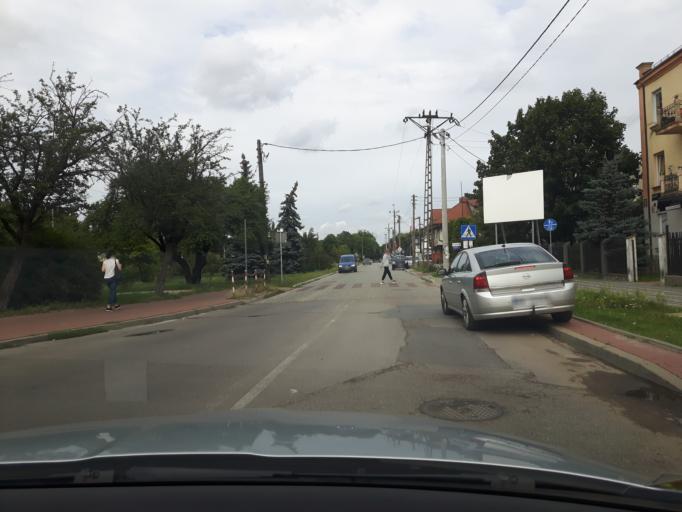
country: PL
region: Masovian Voivodeship
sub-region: Powiat wolominski
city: Zabki
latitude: 52.2916
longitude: 21.1122
